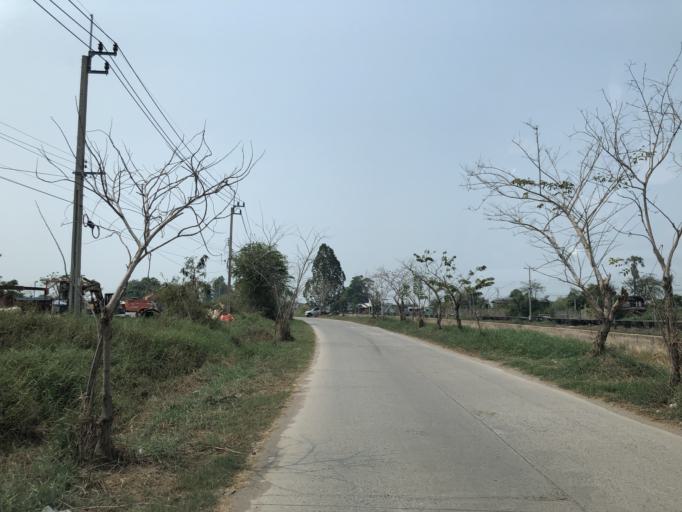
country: TH
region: Samut Prakan
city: Bang Bo
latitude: 13.5197
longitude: 100.8155
